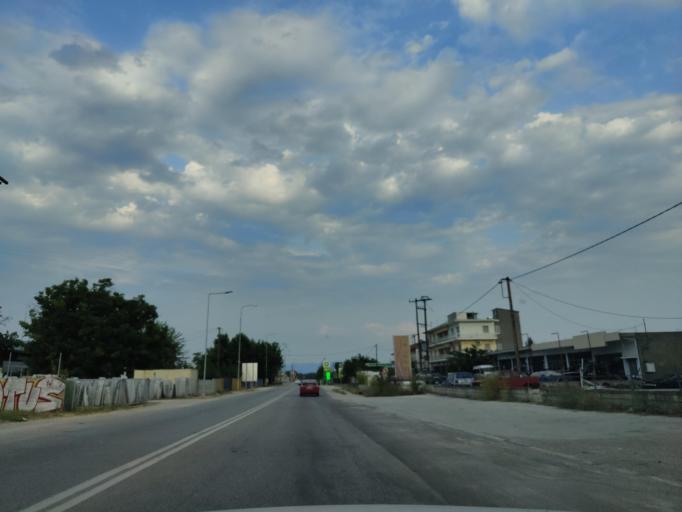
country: GR
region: East Macedonia and Thrace
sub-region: Nomos Dramas
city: Xiropotamos
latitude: 41.1566
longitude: 24.1046
